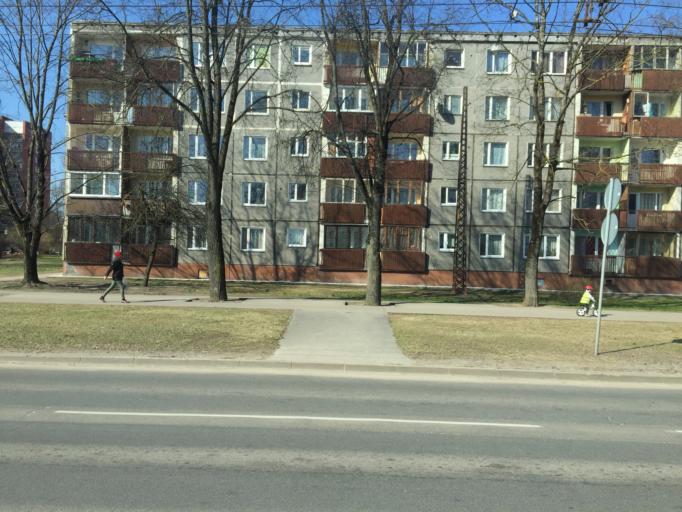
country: LV
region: Marupe
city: Marupe
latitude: 56.9520
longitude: 24.0538
